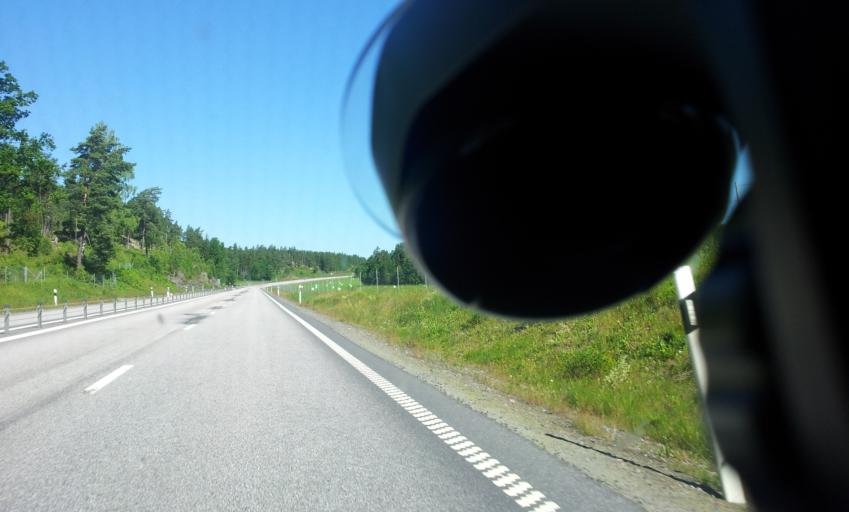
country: SE
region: OEstergoetland
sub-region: Soderkopings Kommun
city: Soederkoeping
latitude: 58.4250
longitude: 16.3890
